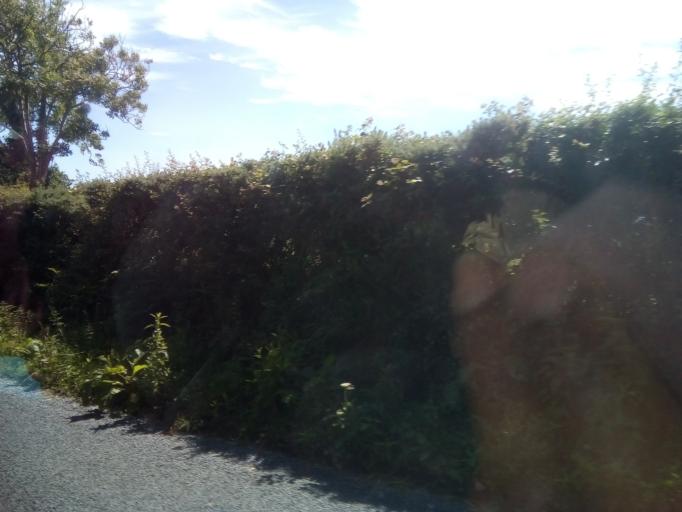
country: IE
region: Leinster
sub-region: Loch Garman
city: Loch Garman
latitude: 52.2523
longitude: -6.6107
